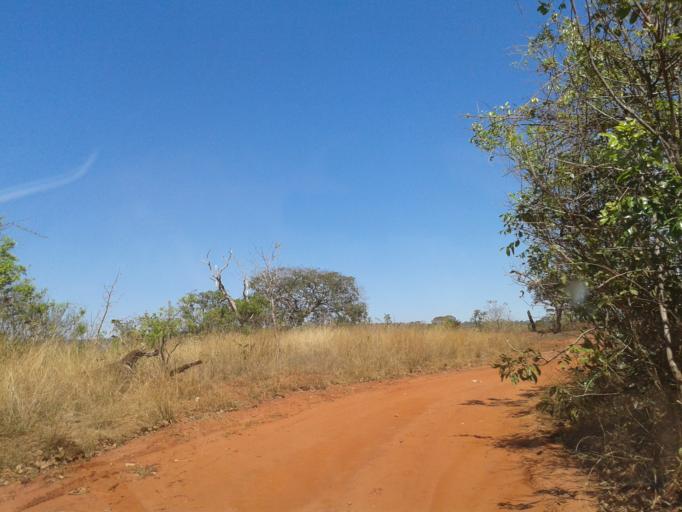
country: BR
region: Minas Gerais
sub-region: Ituiutaba
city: Ituiutaba
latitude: -19.1114
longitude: -49.2843
